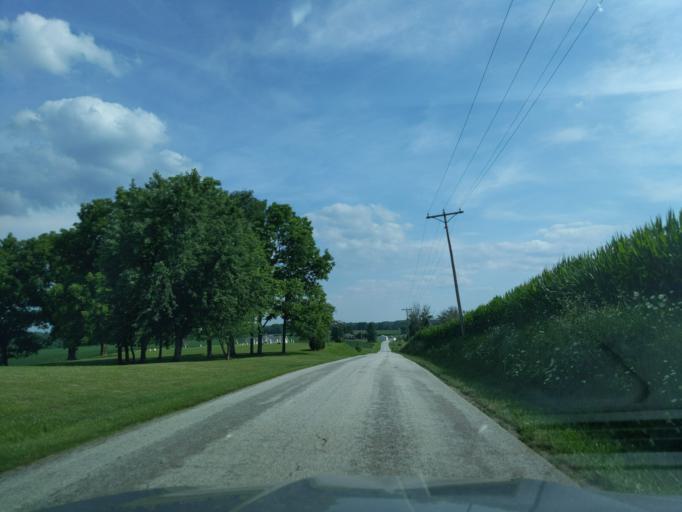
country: US
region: Indiana
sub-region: Decatur County
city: Greensburg
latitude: 39.2681
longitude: -85.4651
